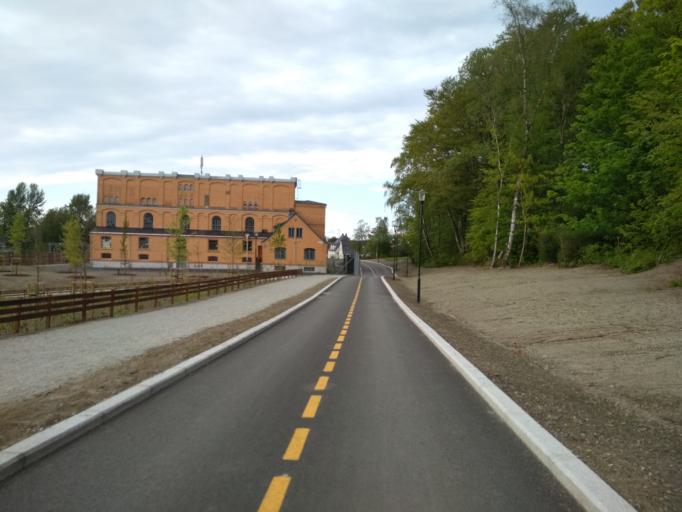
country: NO
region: Rogaland
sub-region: Stavanger
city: Stavanger
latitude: 58.9570
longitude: 5.7239
